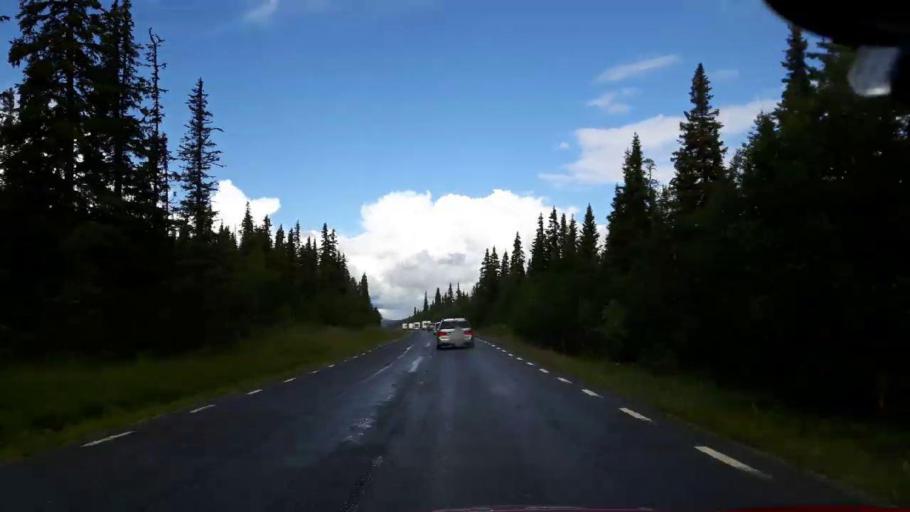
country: SE
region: Vaesterbotten
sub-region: Vilhelmina Kommun
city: Sjoberg
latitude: 65.0254
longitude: 15.1511
